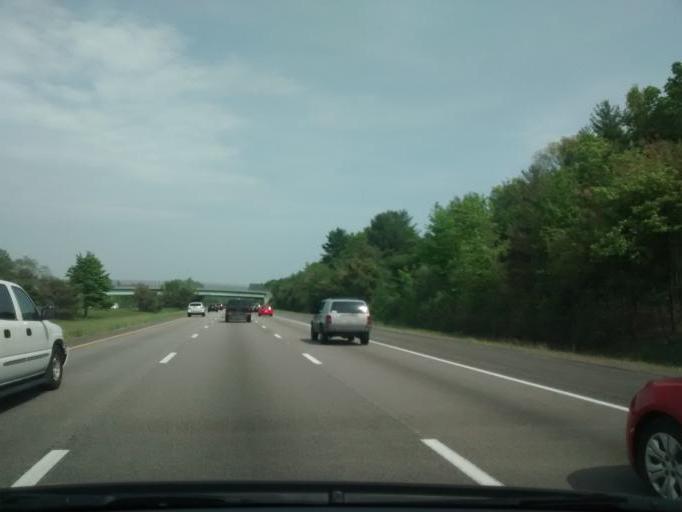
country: US
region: Massachusetts
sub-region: Bristol County
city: Norton Center
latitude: 41.9946
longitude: -71.1871
